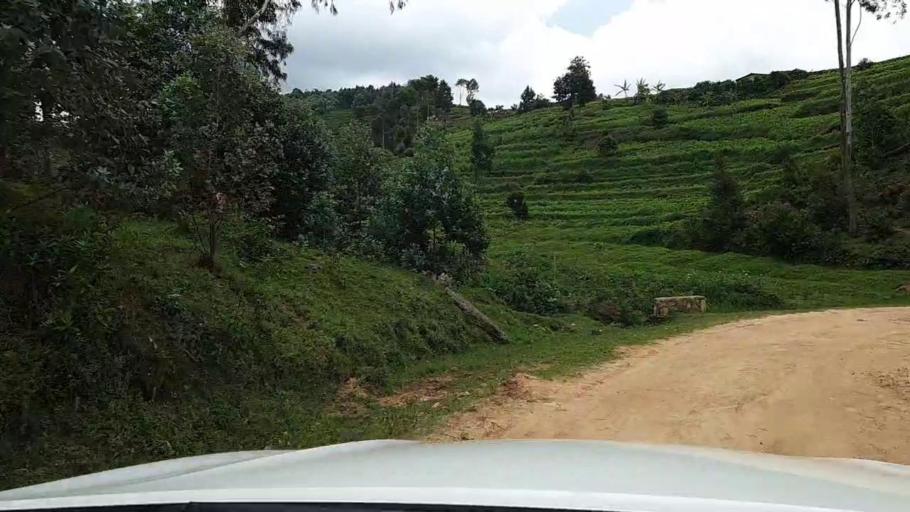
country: RW
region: Western Province
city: Kibuye
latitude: -2.2823
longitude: 29.3679
